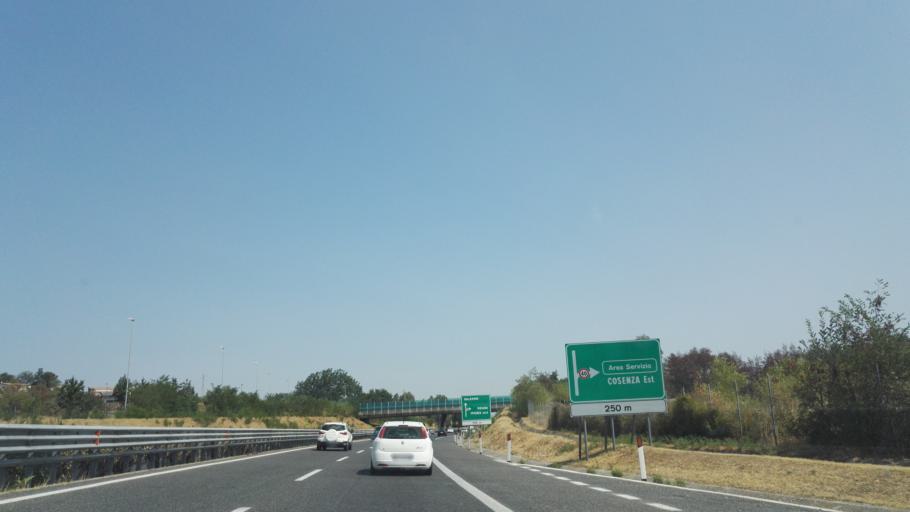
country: IT
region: Calabria
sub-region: Provincia di Cosenza
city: Quattromiglia
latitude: 39.3407
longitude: 16.2348
